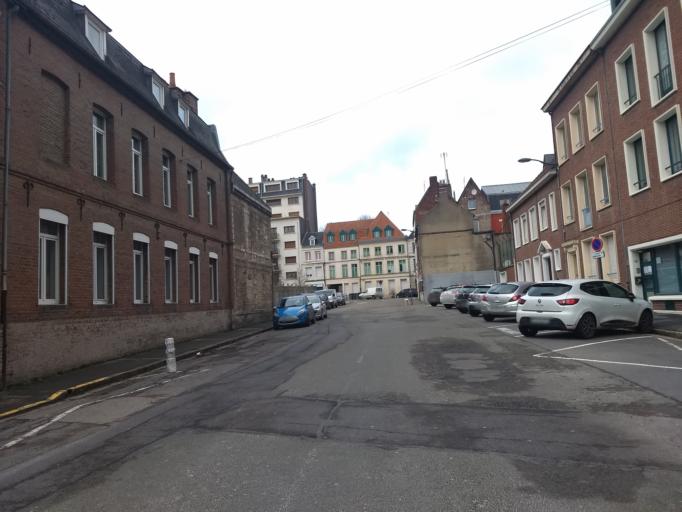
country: FR
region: Nord-Pas-de-Calais
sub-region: Departement du Pas-de-Calais
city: Achicourt
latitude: 50.2900
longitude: 2.7640
